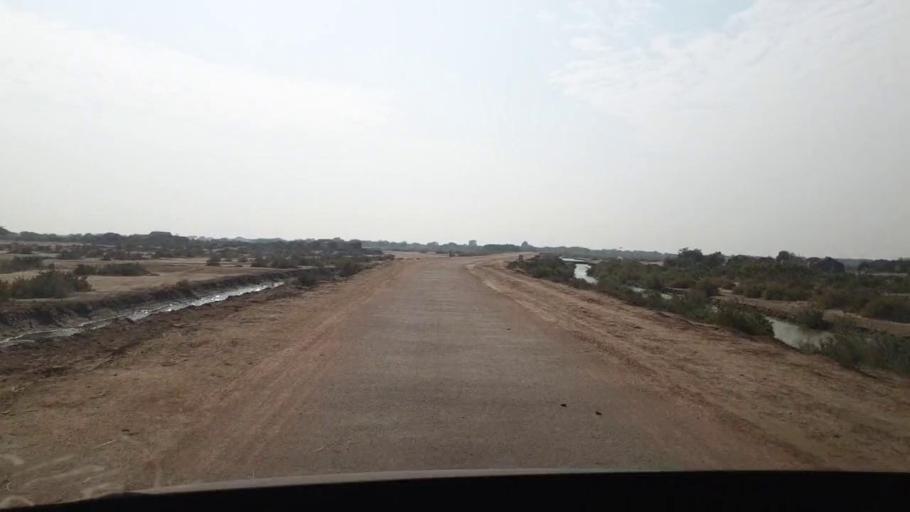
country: PK
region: Sindh
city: Chuhar Jamali
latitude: 24.2438
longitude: 67.9901
